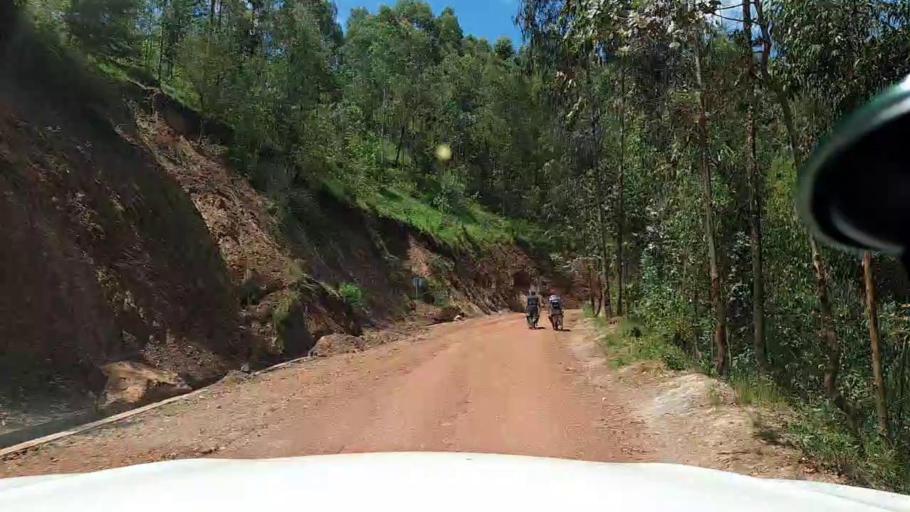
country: RW
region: Northern Province
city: Byumba
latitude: -1.7380
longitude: 29.8584
